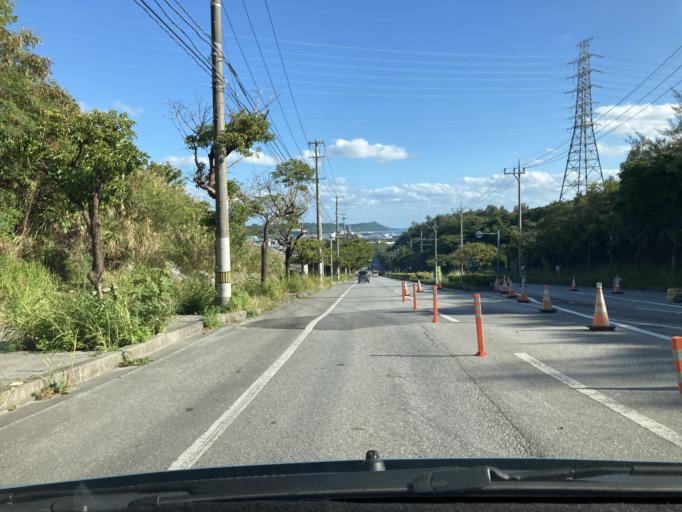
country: JP
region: Okinawa
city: Gushikawa
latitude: 26.3455
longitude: 127.8373
